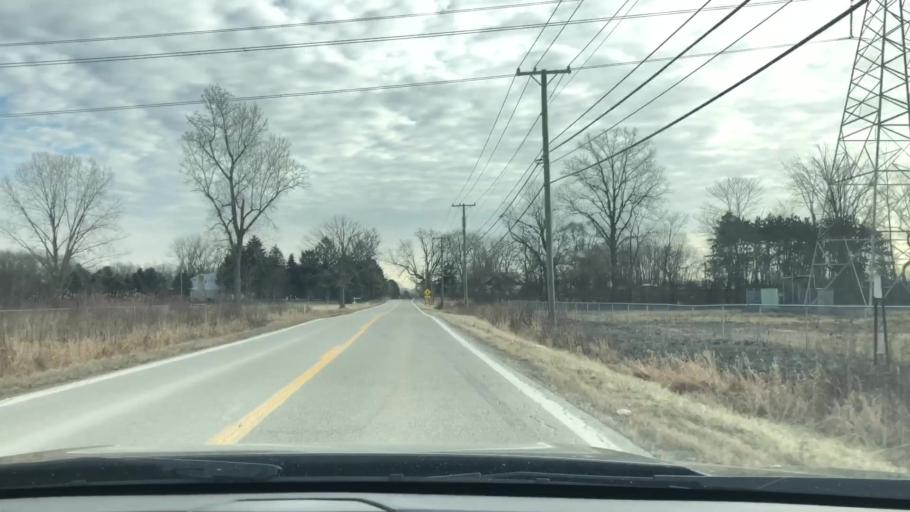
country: US
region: Michigan
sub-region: Macomb County
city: Shelby
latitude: 42.7289
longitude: -83.0081
